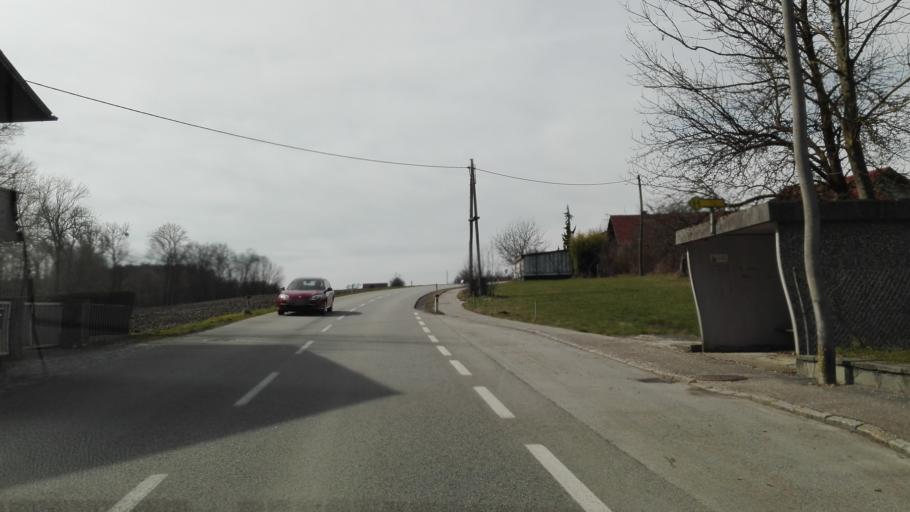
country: AT
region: Upper Austria
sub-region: Politischer Bezirk Scharding
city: Sankt Marienkirchen bei Schaerding
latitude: 48.3712
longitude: 13.5485
